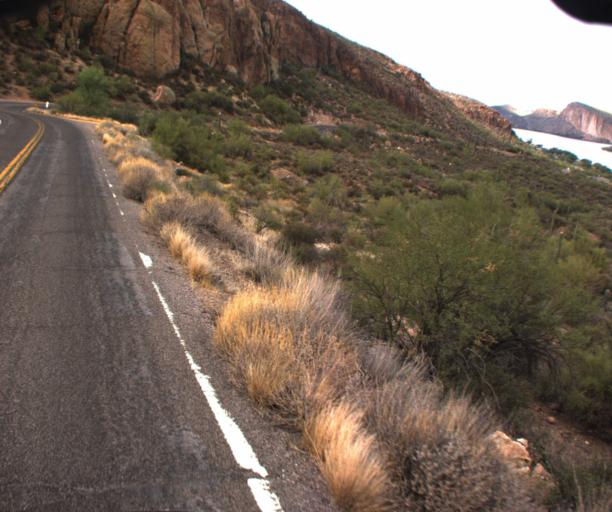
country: US
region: Arizona
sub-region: Pinal County
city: Apache Junction
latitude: 33.5295
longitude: -111.4108
